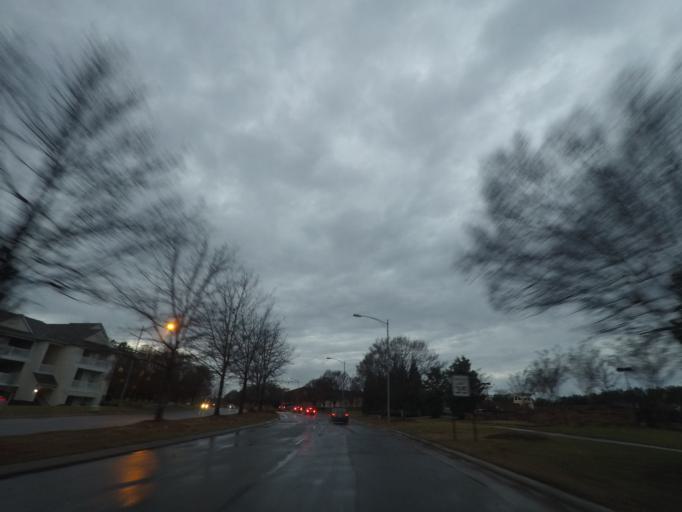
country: US
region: North Carolina
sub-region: Orange County
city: Chapel Hill
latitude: 35.9029
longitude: -78.9542
